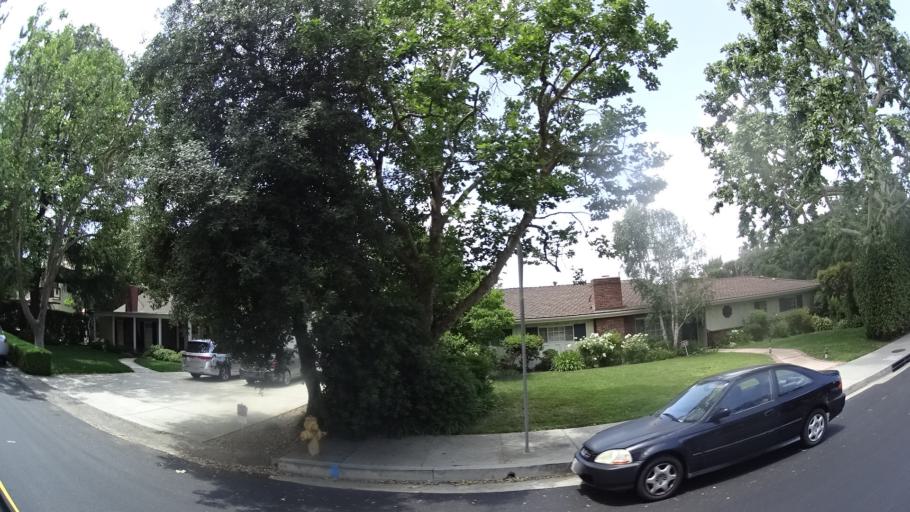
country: US
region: California
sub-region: Los Angeles County
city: Sherman Oaks
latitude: 34.1457
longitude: -118.4213
